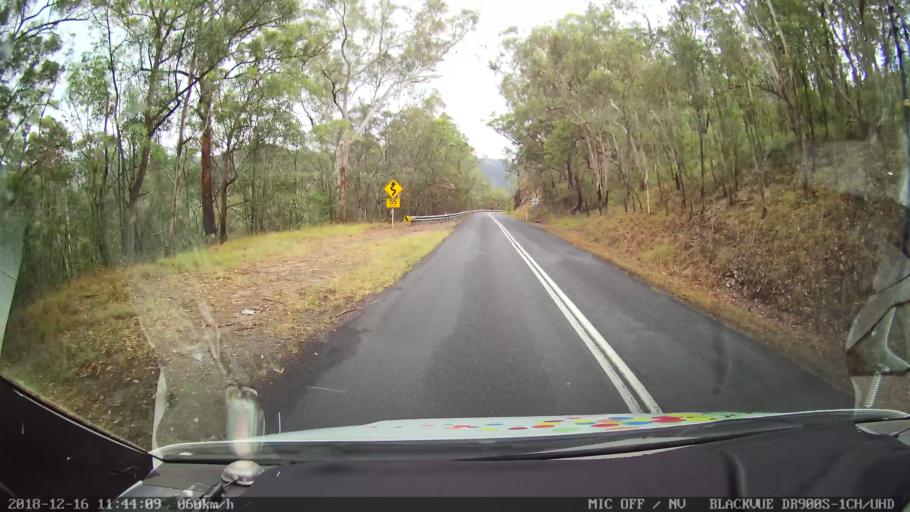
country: AU
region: New South Wales
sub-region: Tenterfield Municipality
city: Carrolls Creek
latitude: -28.9407
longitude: 152.2200
